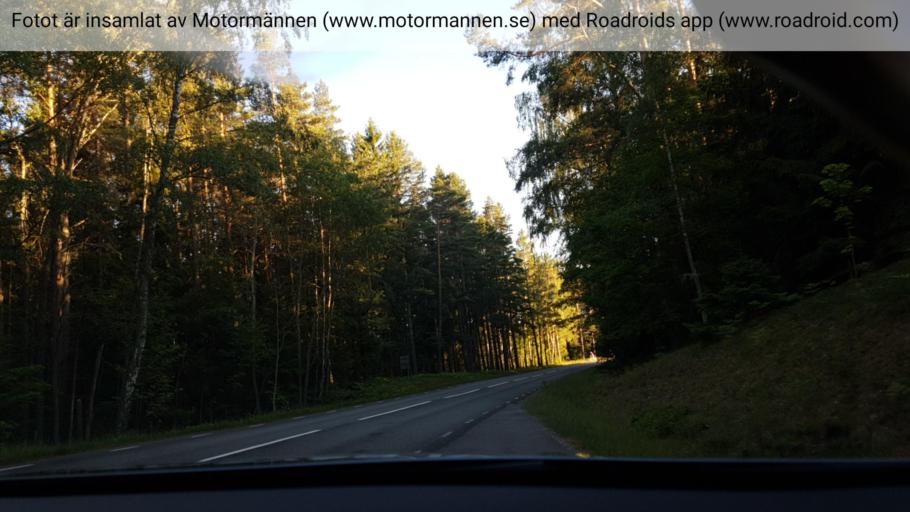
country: SE
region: Vaestra Goetaland
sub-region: Karlsborgs Kommun
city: Molltorp
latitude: 58.4269
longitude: 14.3970
